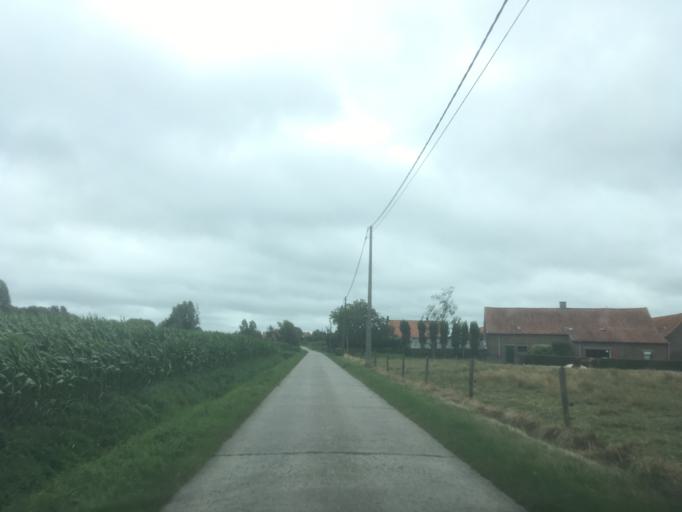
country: BE
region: Flanders
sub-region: Provincie West-Vlaanderen
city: Roeselare
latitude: 50.9228
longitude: 3.1000
